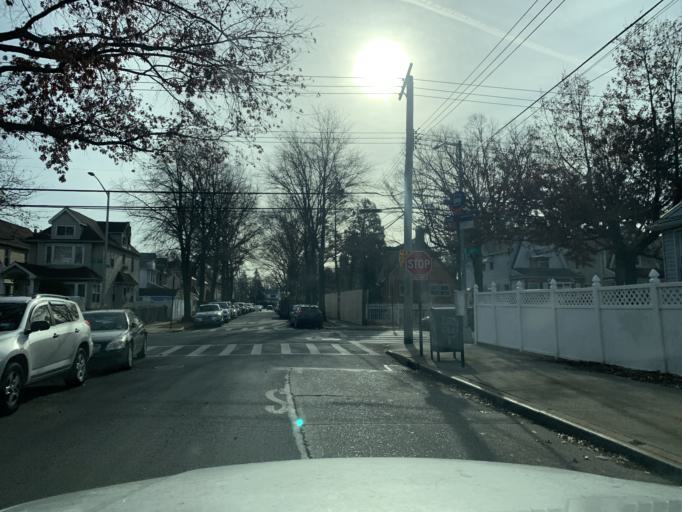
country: US
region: New York
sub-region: Queens County
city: Jamaica
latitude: 40.6959
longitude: -73.7790
